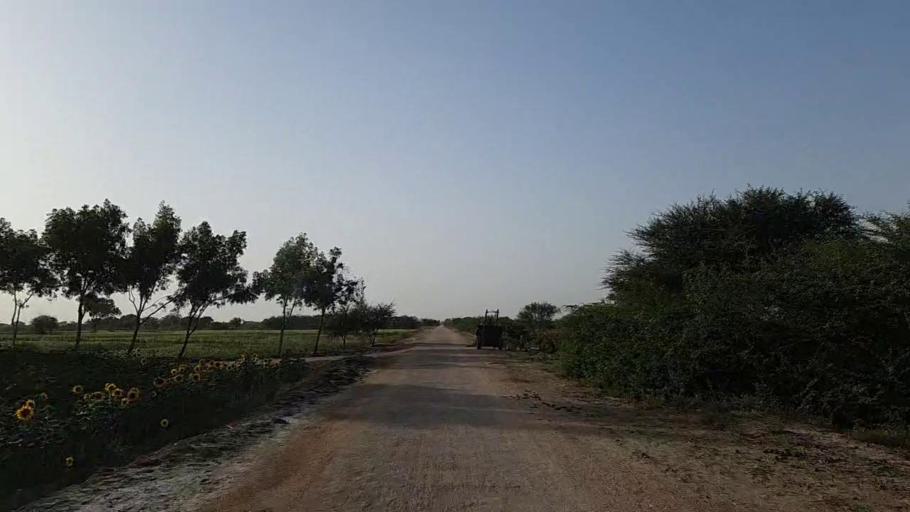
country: PK
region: Sindh
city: Jati
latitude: 24.3299
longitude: 68.1595
